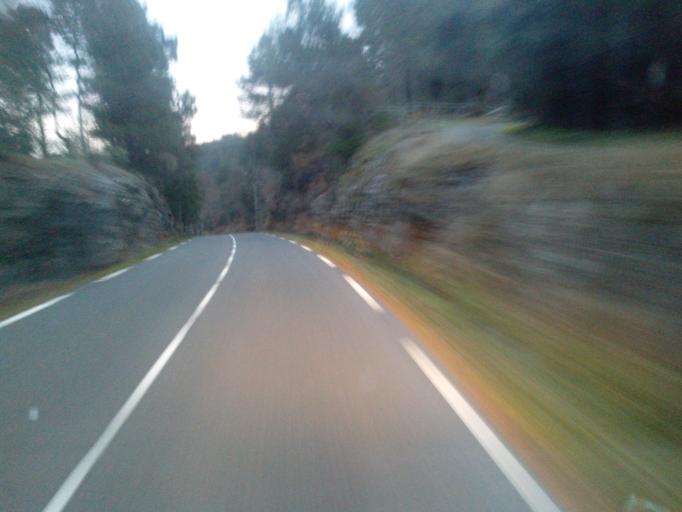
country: FR
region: Languedoc-Roussillon
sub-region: Departement du Gard
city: Saint-Jean-du-Gard
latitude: 44.1400
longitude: 3.7806
